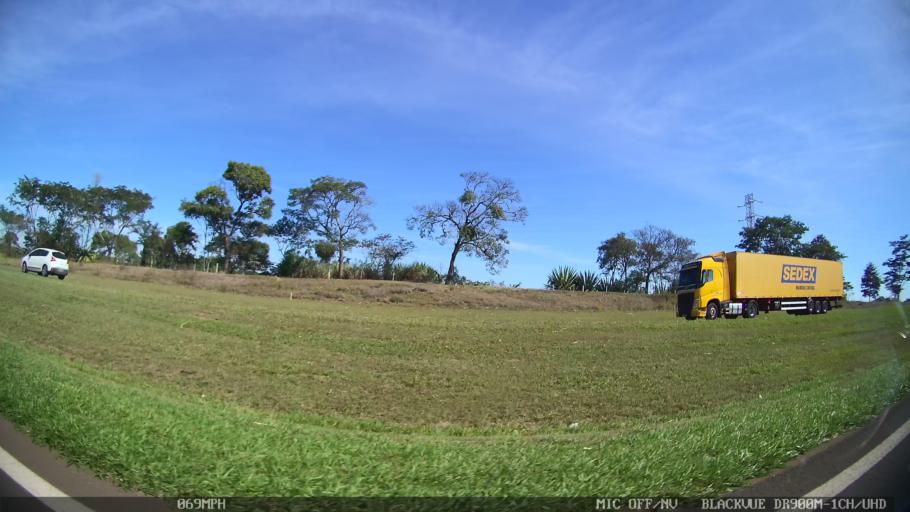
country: BR
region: Sao Paulo
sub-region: Porto Ferreira
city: Porto Ferreira
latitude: -21.8206
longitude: -47.4960
